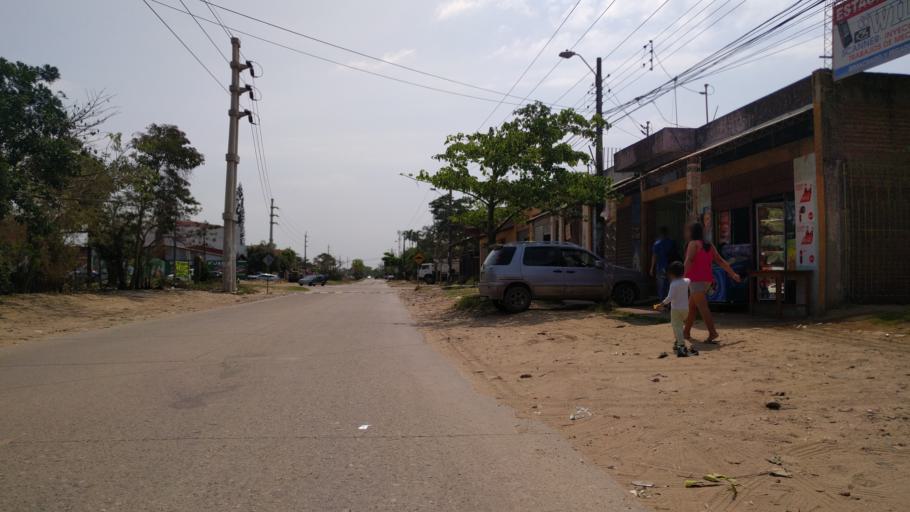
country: BO
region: Santa Cruz
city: Santa Cruz de la Sierra
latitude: -17.8272
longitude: -63.2140
